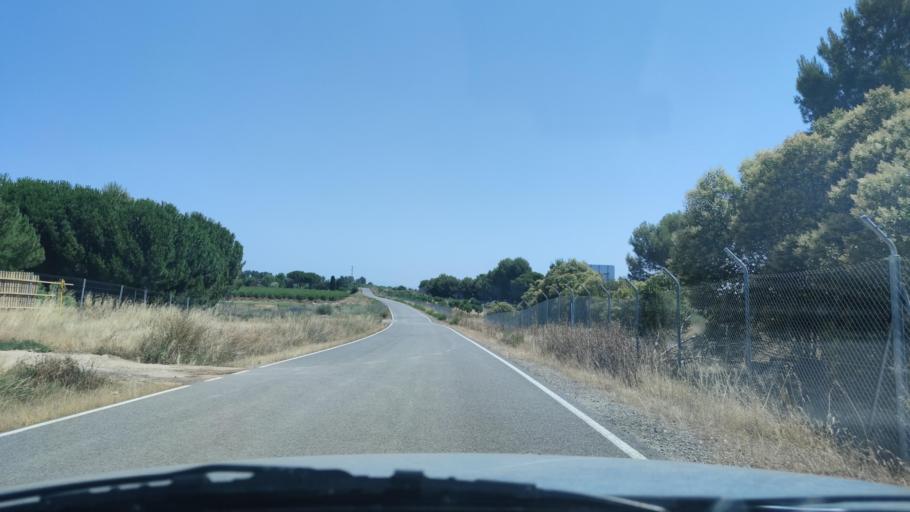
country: ES
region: Catalonia
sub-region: Provincia de Lleida
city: Alpicat
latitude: 41.6509
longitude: 0.5713
